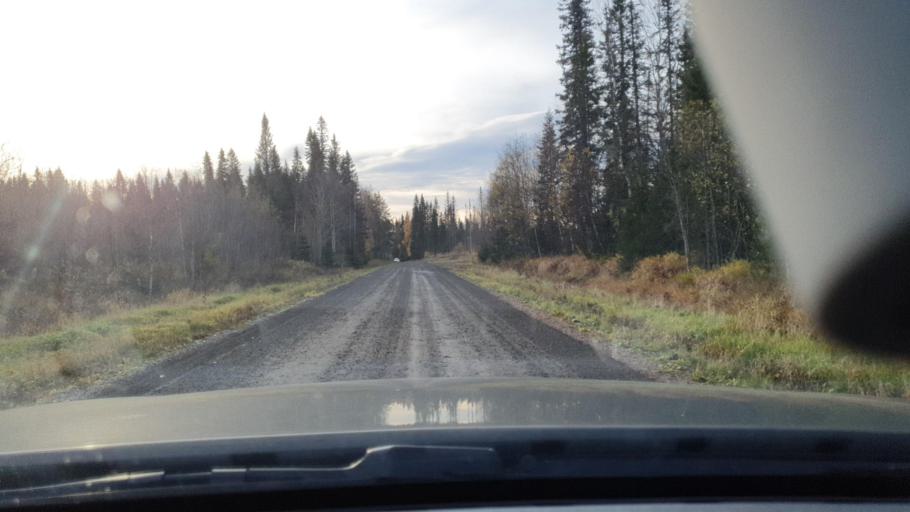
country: SE
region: Jaemtland
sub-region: Stroemsunds Kommun
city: Stroemsund
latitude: 63.5199
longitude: 15.6377
